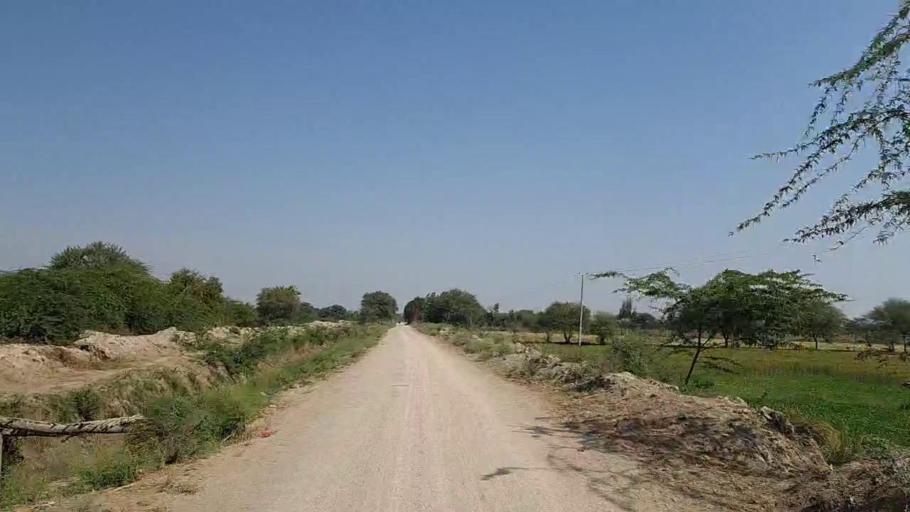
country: PK
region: Sindh
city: Mirpur Batoro
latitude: 24.6859
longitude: 68.2578
